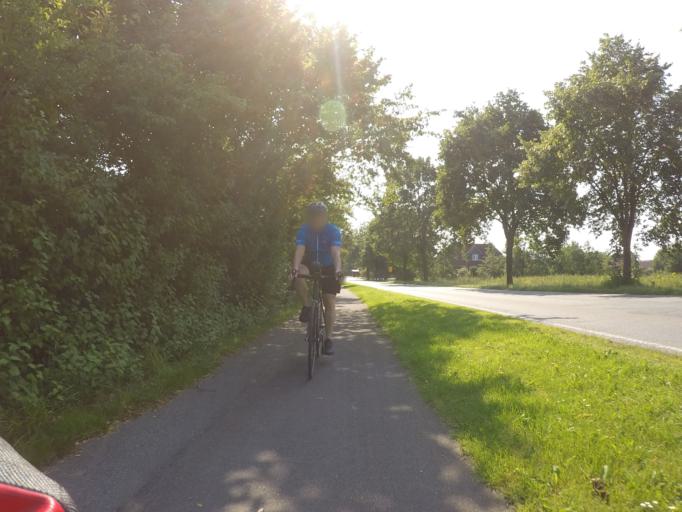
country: DE
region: Schleswig-Holstein
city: Sievershutten
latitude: 53.8426
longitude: 10.1079
